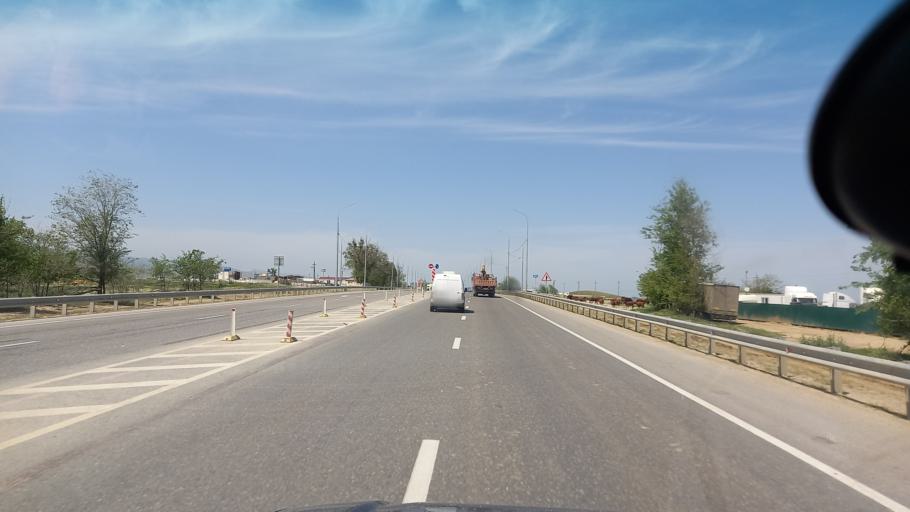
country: RU
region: Dagestan
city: Manas
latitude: 42.7282
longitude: 47.6659
